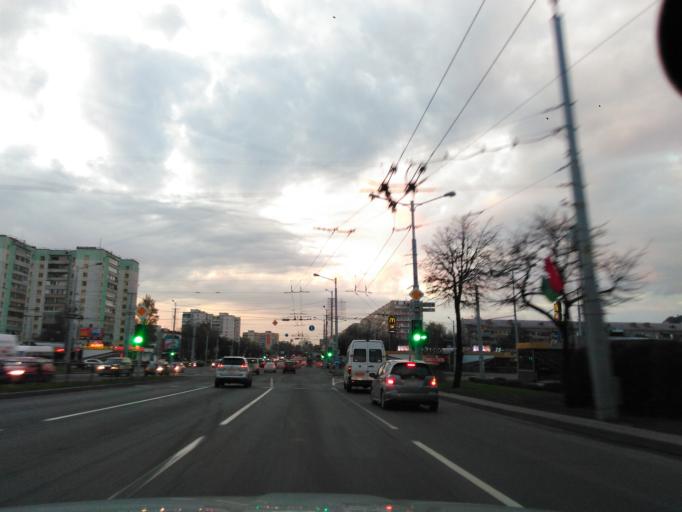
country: BY
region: Minsk
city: Novoye Medvezhino
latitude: 53.9085
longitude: 27.4959
